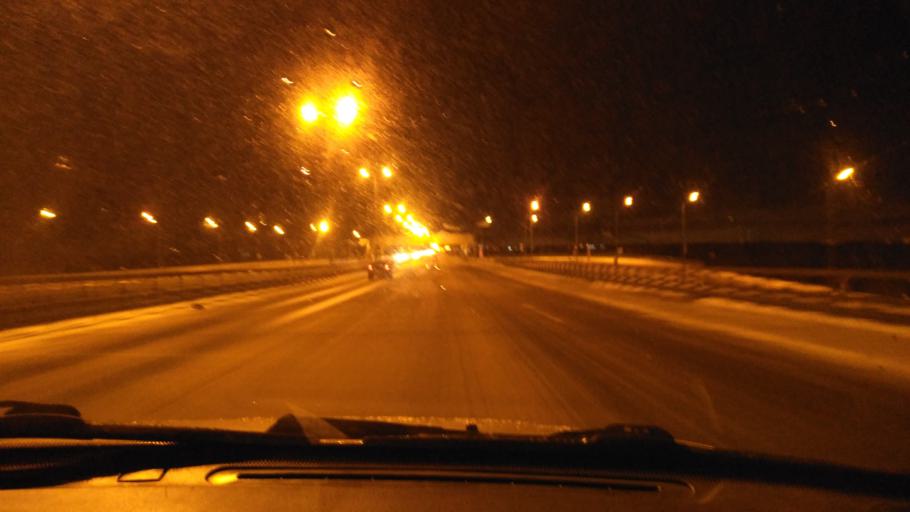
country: RU
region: St.-Petersburg
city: Kronshtadt
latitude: 60.0269
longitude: 29.8443
